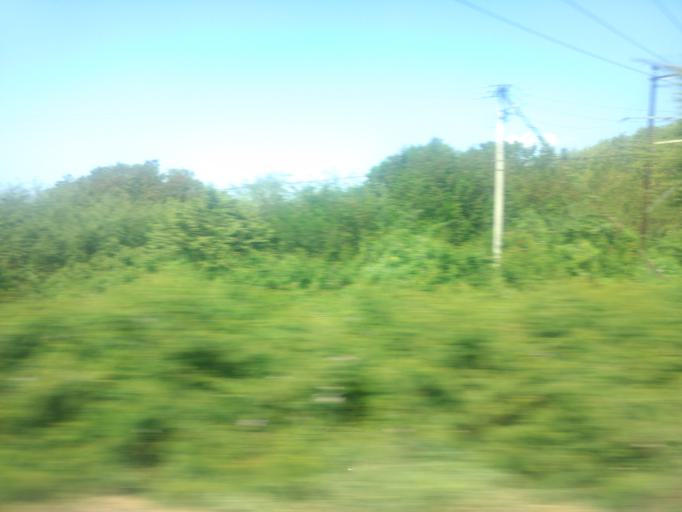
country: MX
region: Colima
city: El Colomo
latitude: 19.0469
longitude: -104.2622
